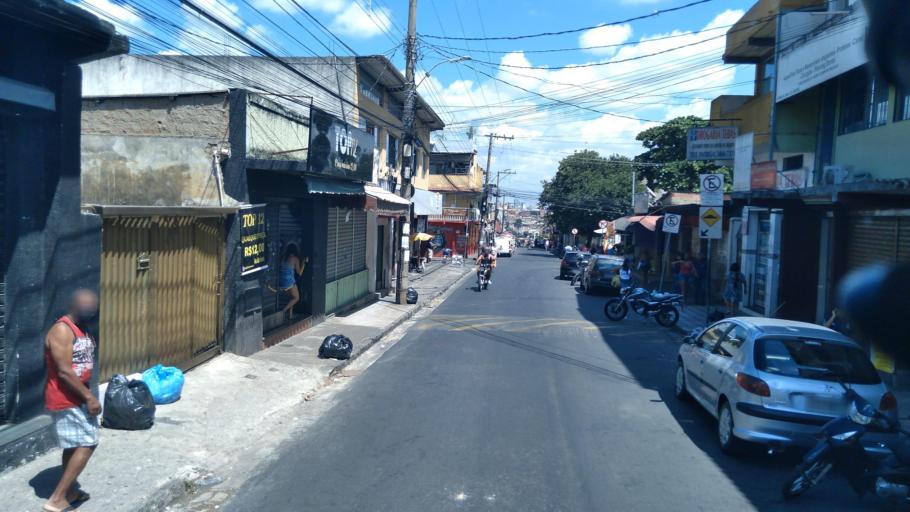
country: BR
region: Minas Gerais
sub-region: Belo Horizonte
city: Belo Horizonte
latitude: -19.9082
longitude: -43.8912
